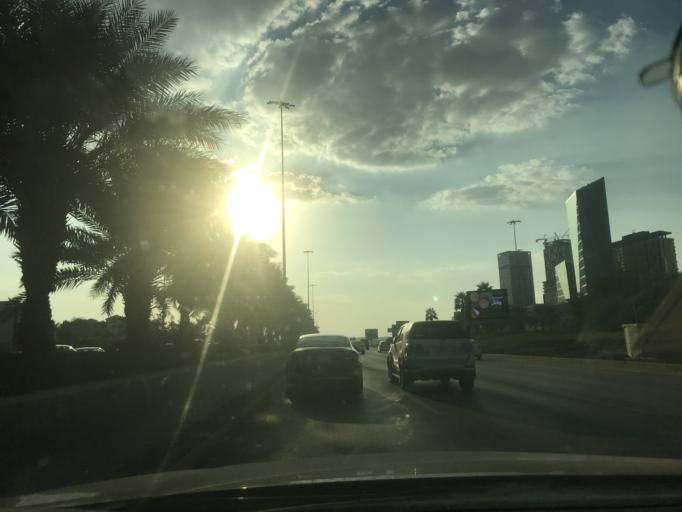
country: SA
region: Ar Riyad
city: Riyadh
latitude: 24.7606
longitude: 46.6460
